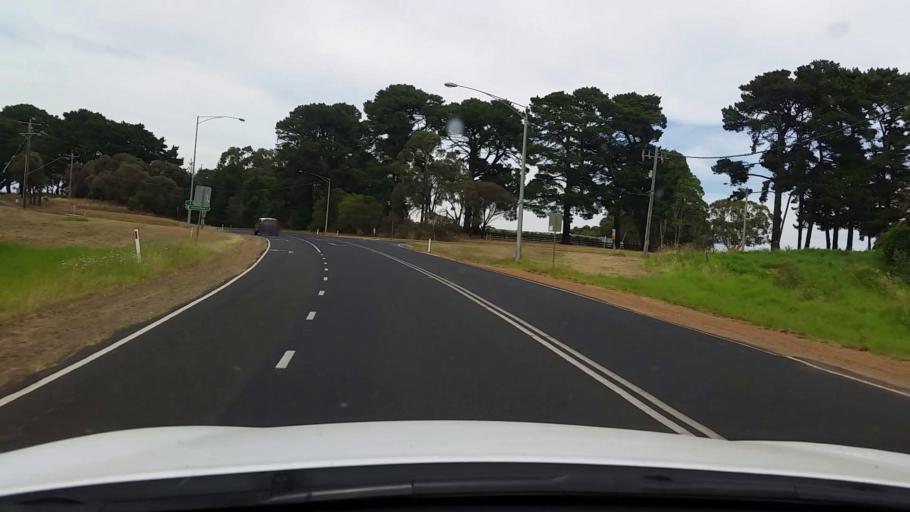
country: AU
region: Victoria
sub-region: Mornington Peninsula
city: Merricks
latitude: -38.4191
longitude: 145.0446
